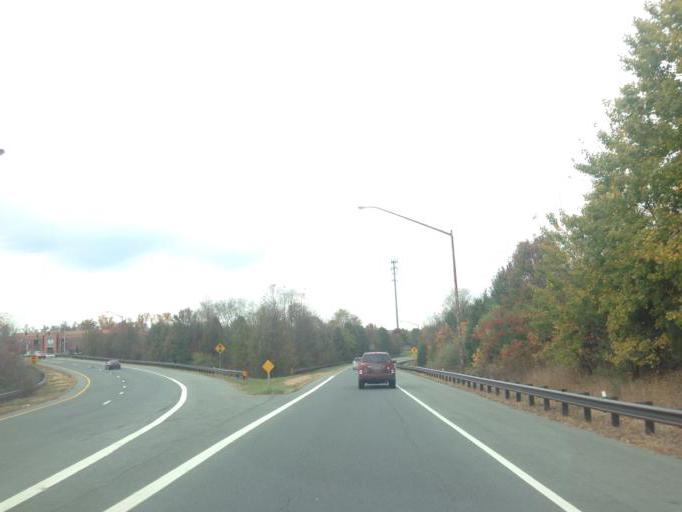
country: US
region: Maryland
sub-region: Montgomery County
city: Germantown
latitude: 39.1973
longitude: -77.2601
